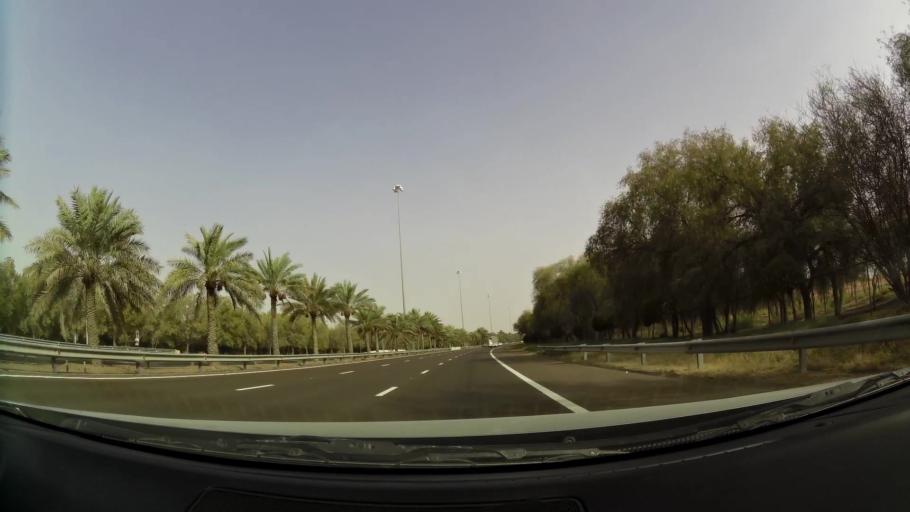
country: AE
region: Abu Dhabi
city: Al Ain
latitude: 24.1964
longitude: 55.5882
